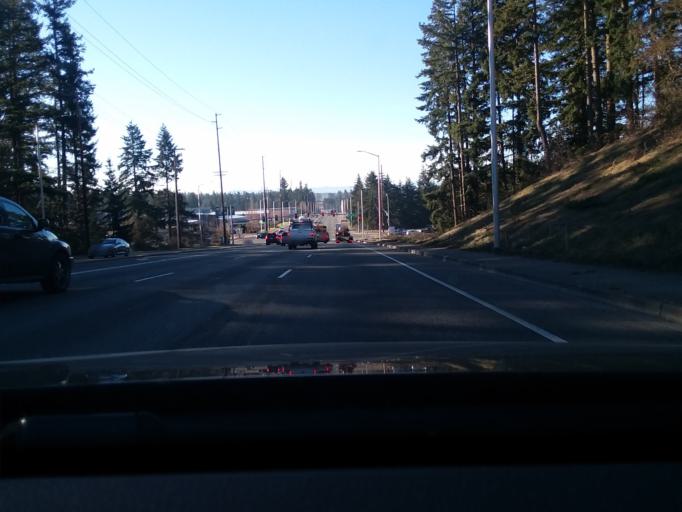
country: US
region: Washington
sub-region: Pierce County
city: Frederickson
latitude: 47.1124
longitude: -122.3577
